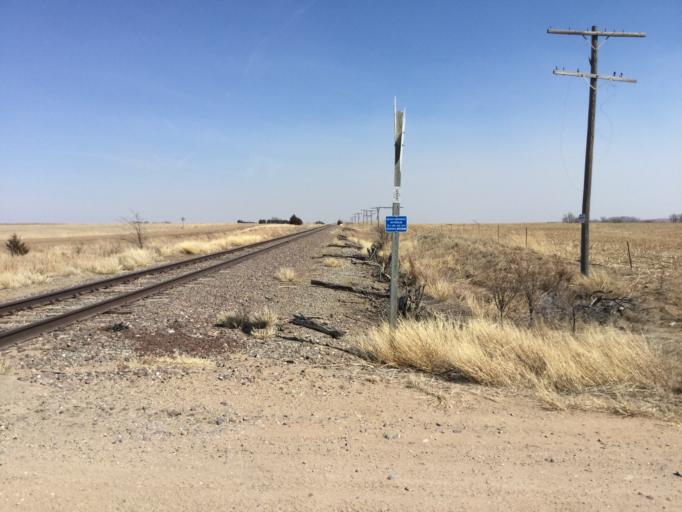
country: US
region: Kansas
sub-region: Rush County
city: La Crosse
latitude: 38.5234
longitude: -99.2725
